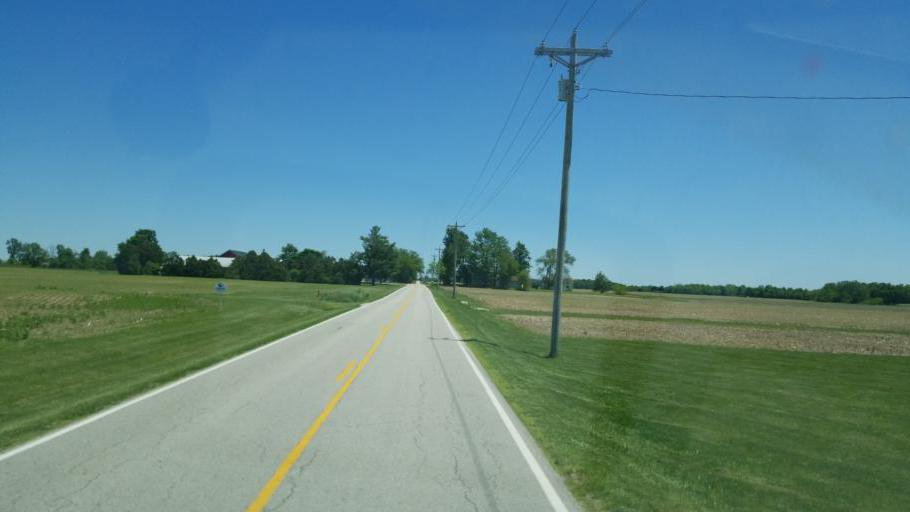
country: US
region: Ohio
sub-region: Darke County
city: Ansonia
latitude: 40.2648
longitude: -84.6732
